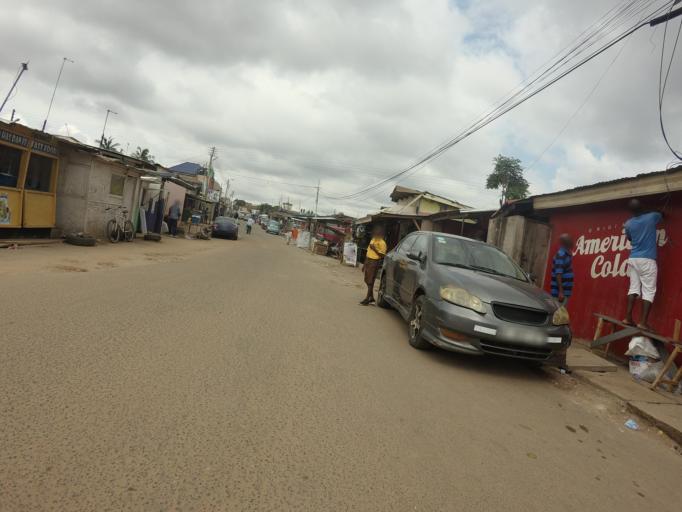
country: GH
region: Greater Accra
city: Accra
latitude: 5.5879
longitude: -0.1999
